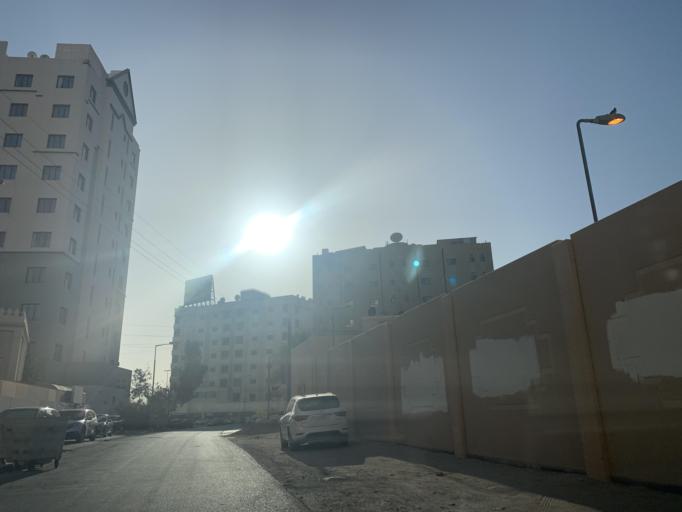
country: BH
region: Manama
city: Manama
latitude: 26.2037
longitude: 50.5836
